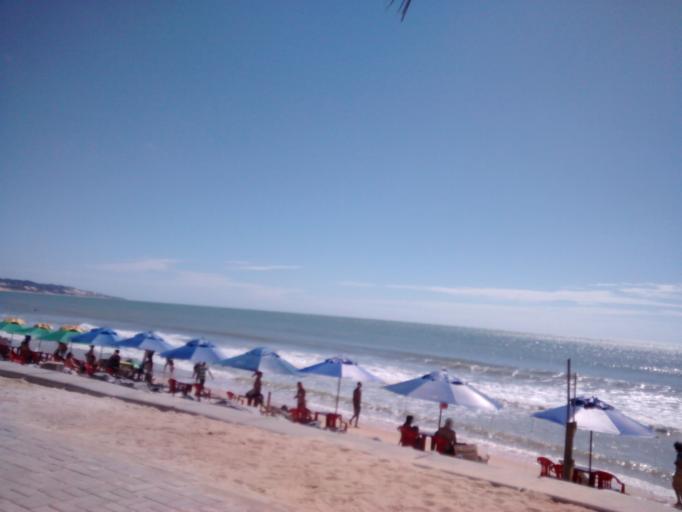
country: BR
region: Rio Grande do Norte
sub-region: Natal
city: Natal
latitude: -5.8795
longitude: -35.1732
